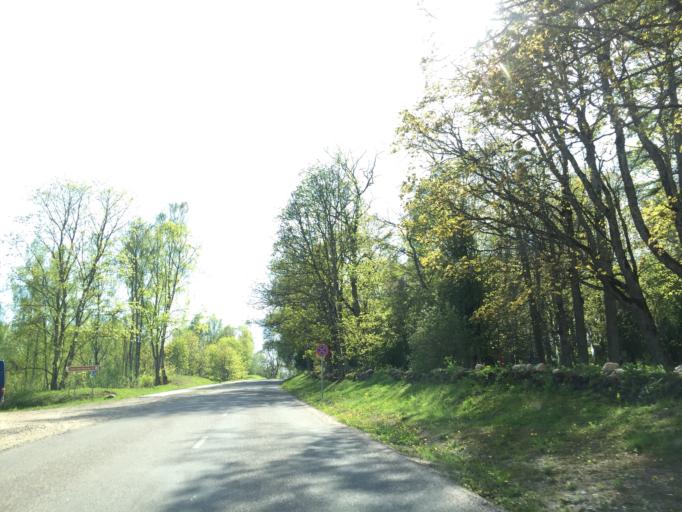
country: LV
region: Limbazu Rajons
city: Limbazi
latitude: 57.5085
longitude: 24.6961
